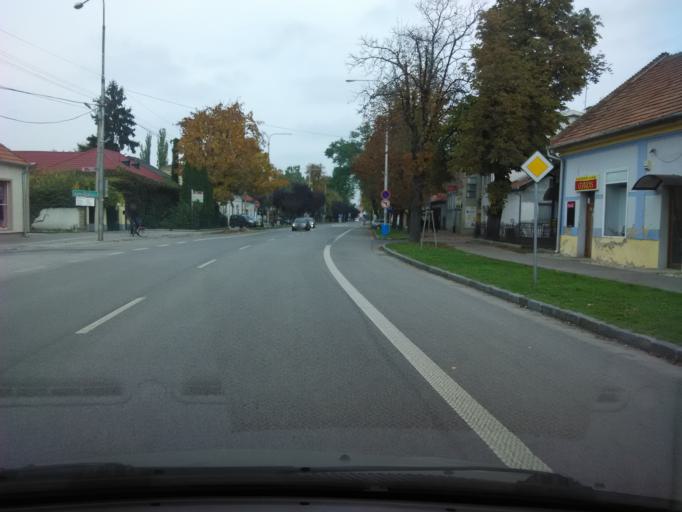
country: SK
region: Nitriansky
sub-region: Okres Komarno
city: Hurbanovo
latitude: 47.8708
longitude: 18.1905
